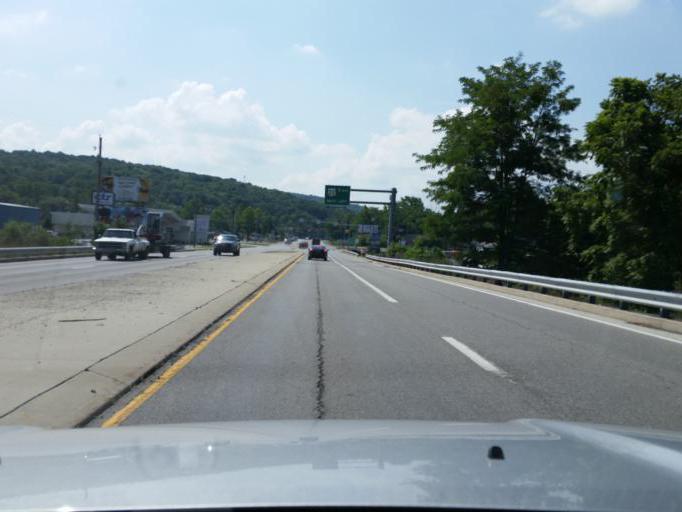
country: US
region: Pennsylvania
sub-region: Blair County
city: Duncansville
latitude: 40.4238
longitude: -78.4411
